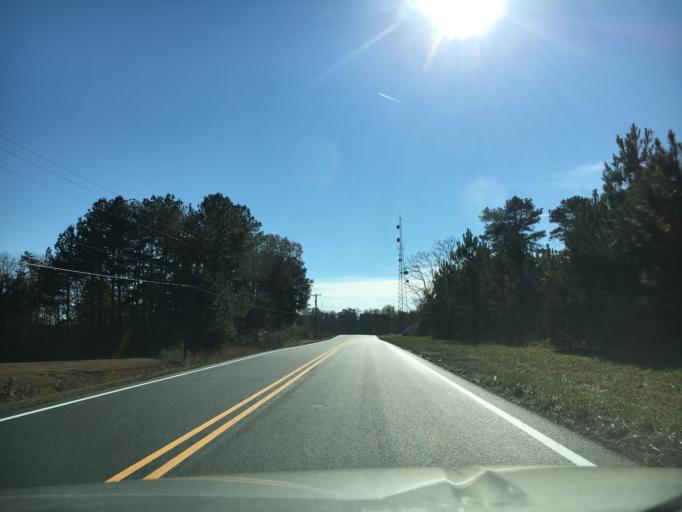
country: US
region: Virginia
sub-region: Cumberland County
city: Cumberland
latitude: 37.4694
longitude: -78.2806
